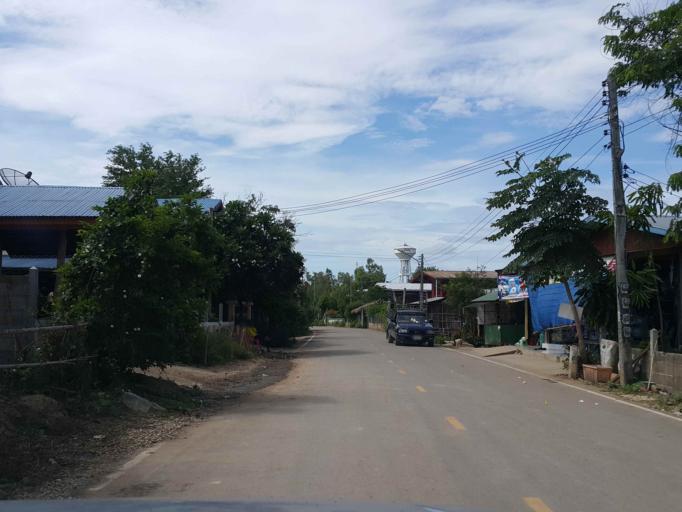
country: TH
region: Sukhothai
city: Ban Dan Lan Hoi
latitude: 17.1082
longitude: 99.4757
